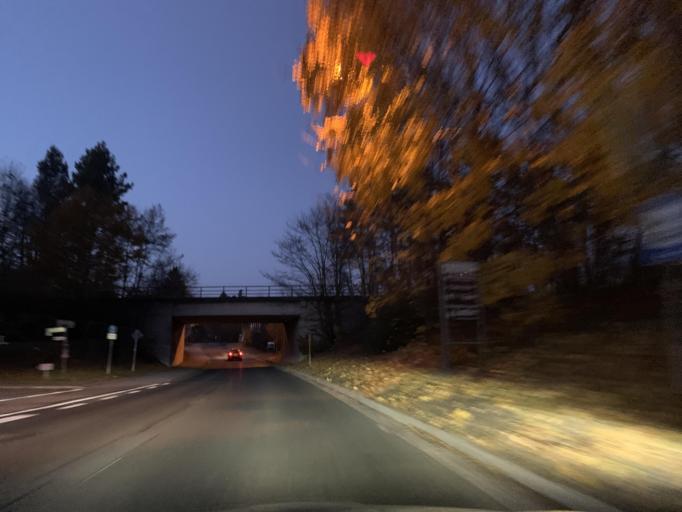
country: DE
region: Bavaria
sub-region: Upper Palatinate
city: Bodenwohr
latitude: 49.2766
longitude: 12.3299
